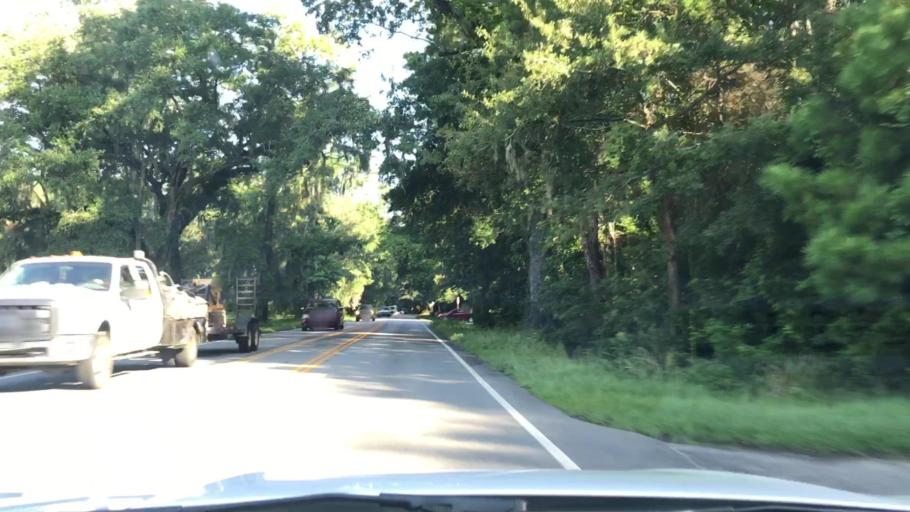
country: US
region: South Carolina
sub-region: Charleston County
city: Shell Point
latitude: 32.8514
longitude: -80.0673
